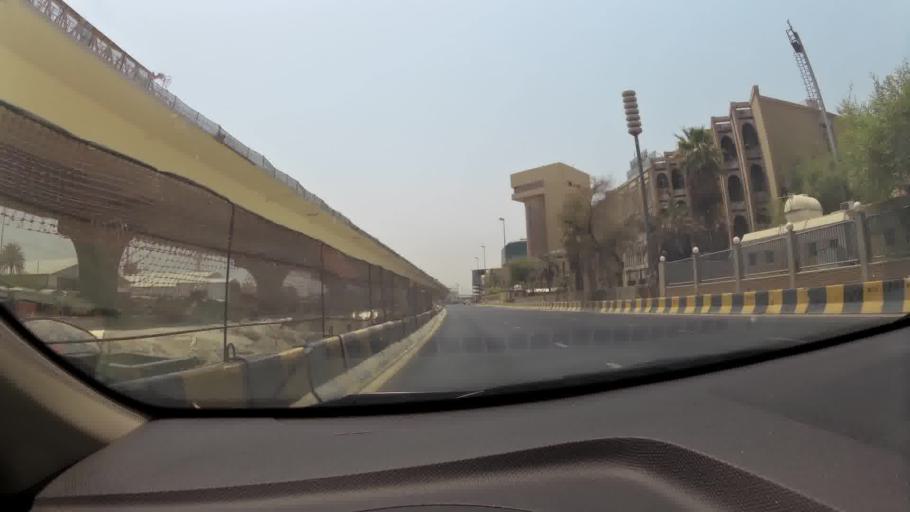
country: KW
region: Al Asimah
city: Ash Shamiyah
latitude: 29.3486
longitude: 47.9389
